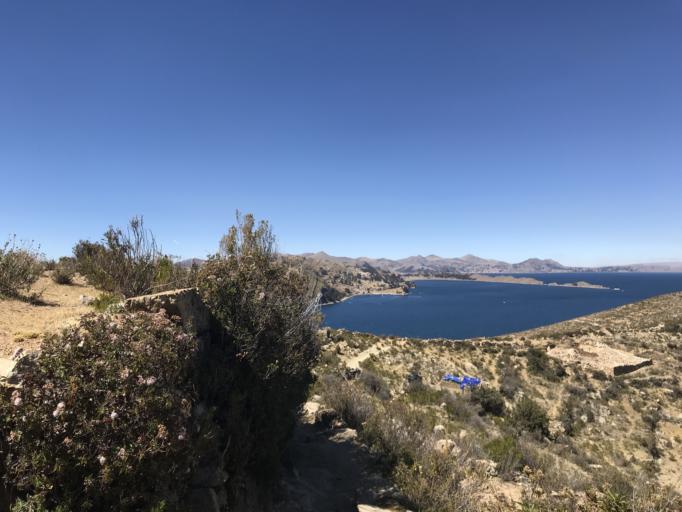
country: BO
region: La Paz
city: Yumani
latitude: -16.0440
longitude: -69.1465
